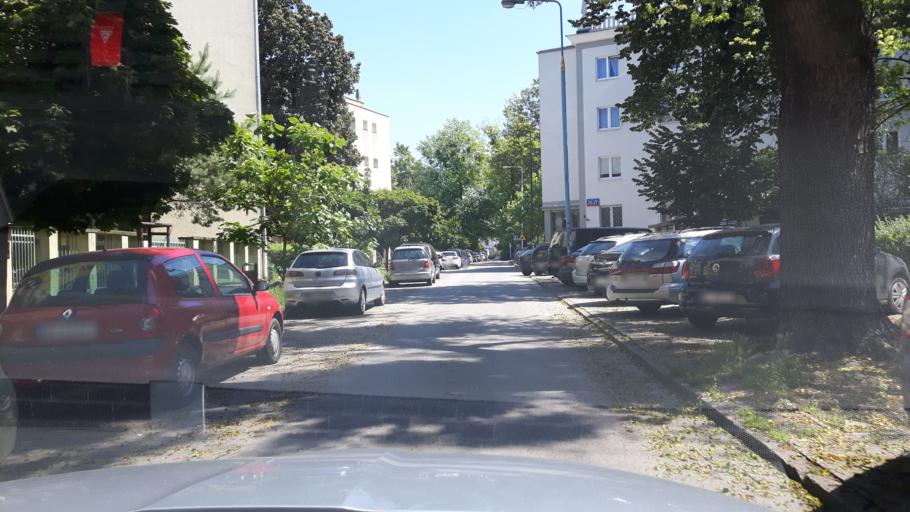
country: PL
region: Masovian Voivodeship
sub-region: Warszawa
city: Ochota
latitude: 52.2158
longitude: 20.9724
